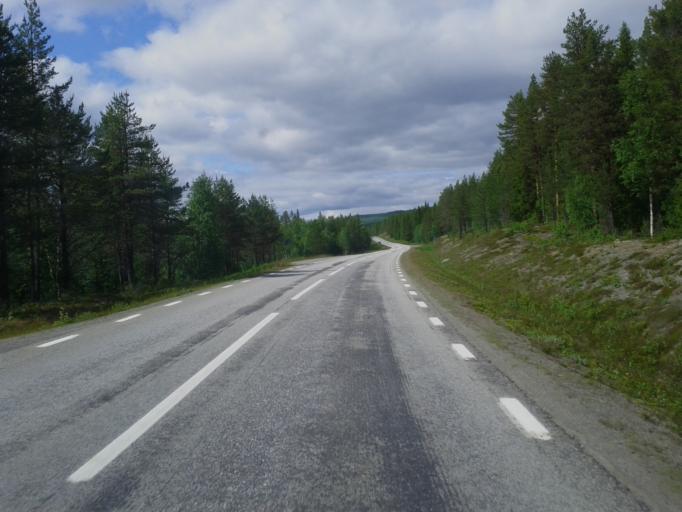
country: SE
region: Vaesterbotten
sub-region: Storumans Kommun
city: Fristad
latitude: 65.3844
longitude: 16.4875
